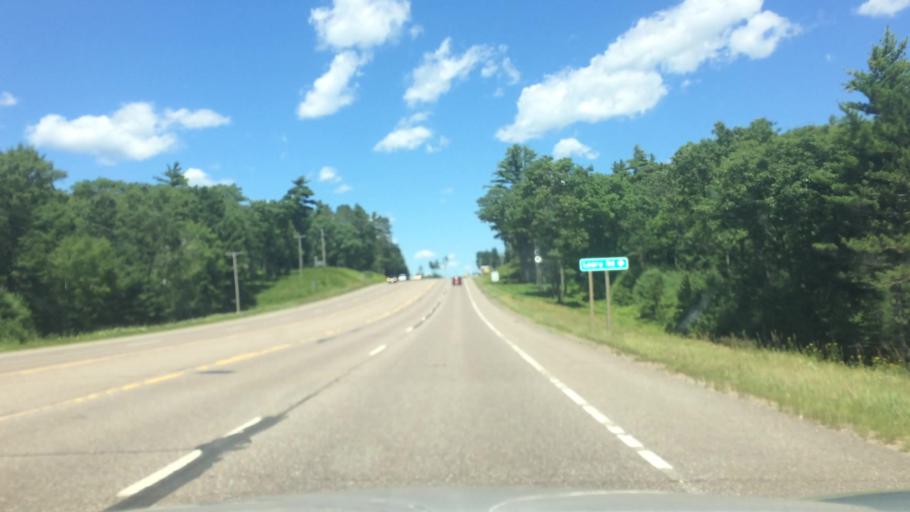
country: US
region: Wisconsin
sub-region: Vilas County
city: Lac du Flambeau
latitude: 45.8462
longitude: -89.7050
